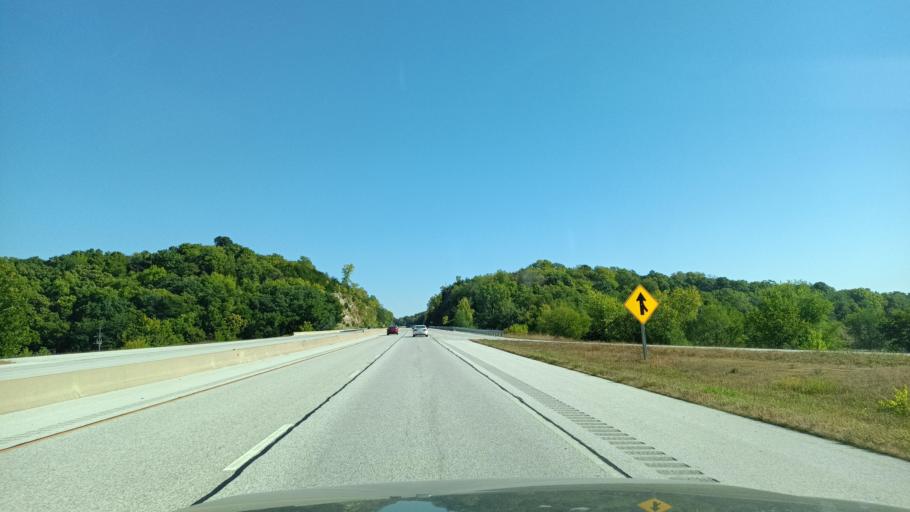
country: US
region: Illinois
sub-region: Adams County
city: Payson
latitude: 39.7869
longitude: -91.3093
